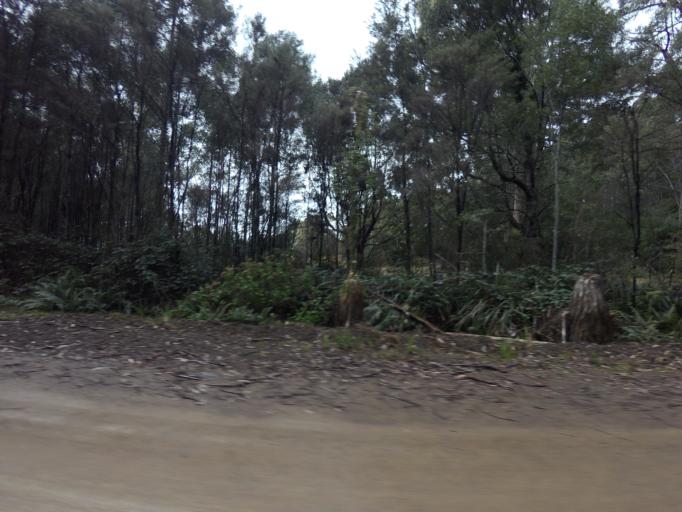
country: AU
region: Tasmania
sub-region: Huon Valley
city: Geeveston
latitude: -43.5499
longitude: 146.8867
